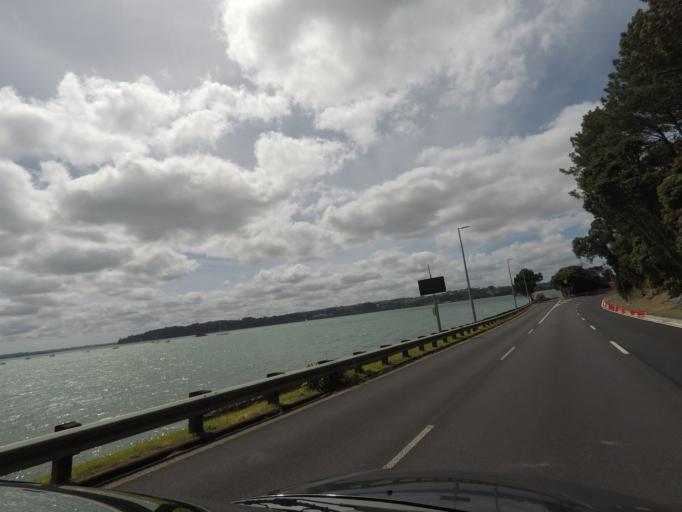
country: NZ
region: Auckland
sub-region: Auckland
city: Auckland
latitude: -36.8395
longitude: 174.7395
